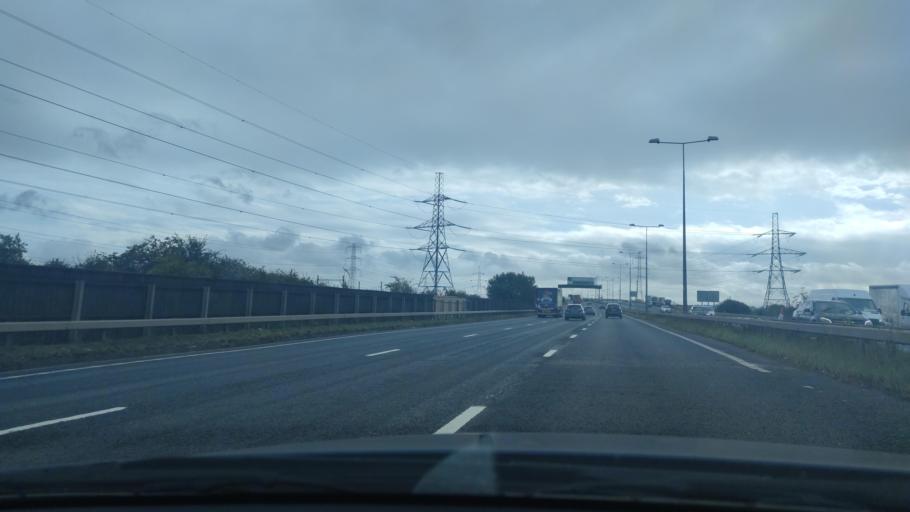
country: GB
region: England
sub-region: Greater London
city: Erith
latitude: 51.5051
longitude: 0.2076
